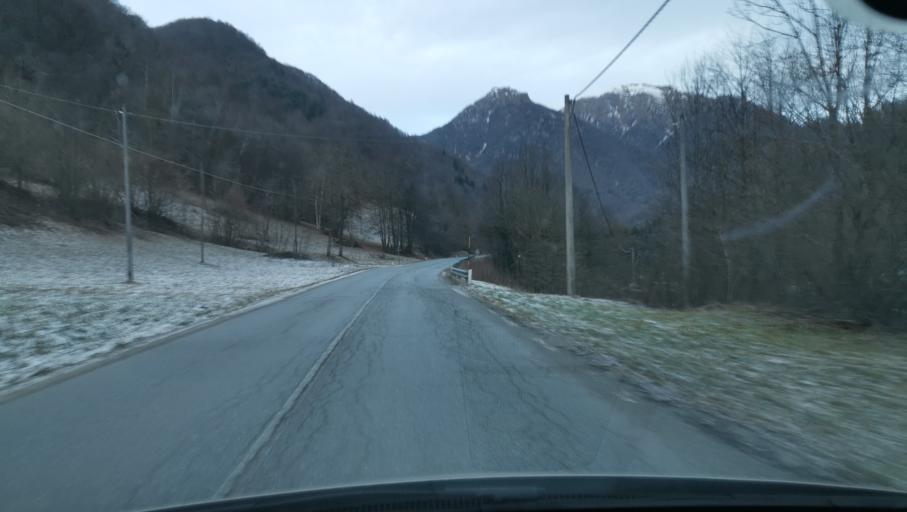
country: IT
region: Piedmont
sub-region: Provincia di Cuneo
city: Pradleves
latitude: 44.4102
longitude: 7.2991
